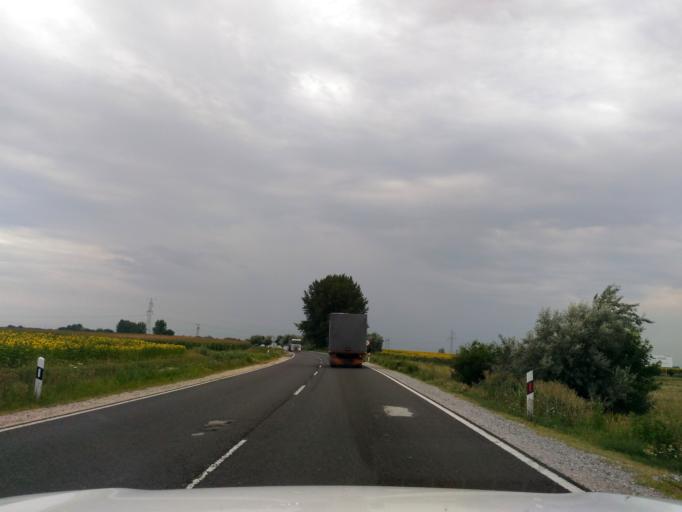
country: HU
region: Jasz-Nagykun-Szolnok
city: Toszeg
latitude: 47.1640
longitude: 20.1056
